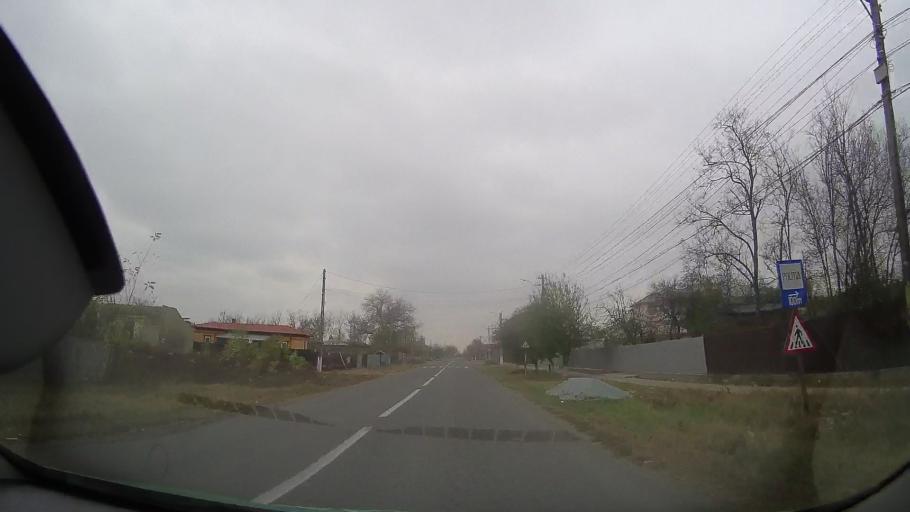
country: RO
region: Ialomita
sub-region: Comuna Garbovi
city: Garbovi
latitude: 44.7850
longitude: 26.7653
